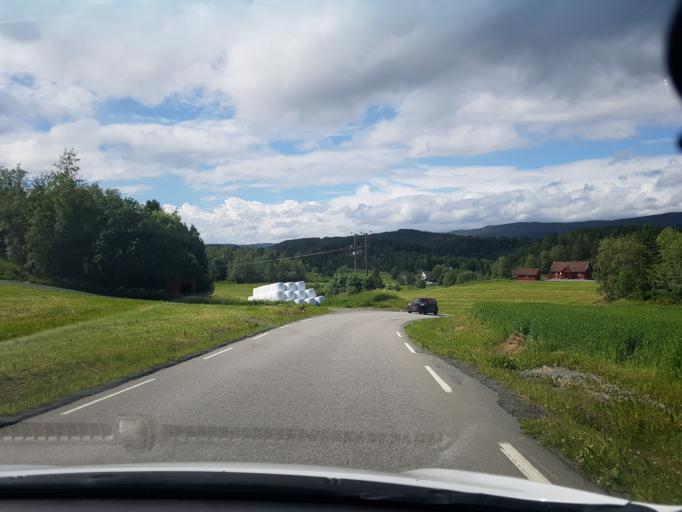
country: NO
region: Nord-Trondelag
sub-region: Stjordal
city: Stjordalshalsen
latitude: 63.5934
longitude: 10.9788
